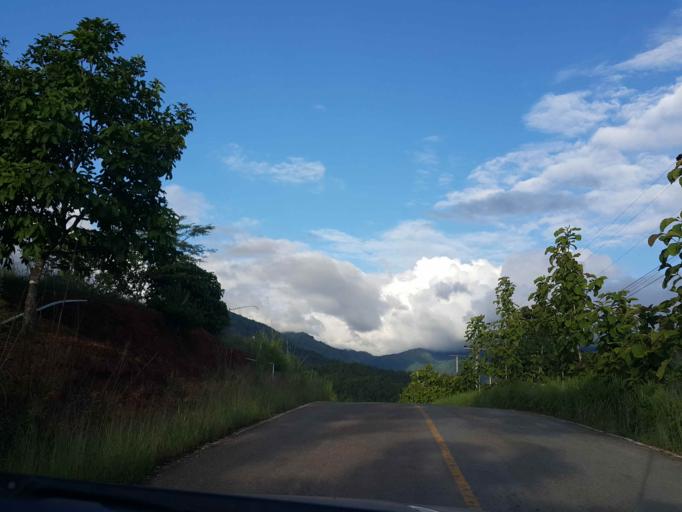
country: TH
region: Chiang Mai
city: Mae Chaem
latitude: 18.5114
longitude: 98.4091
